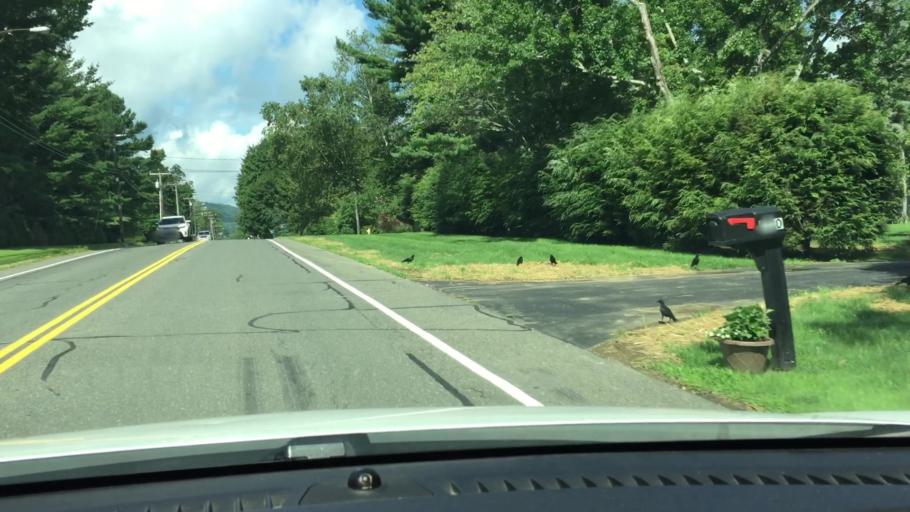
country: US
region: Massachusetts
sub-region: Berkshire County
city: Pittsfield
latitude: 42.4533
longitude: -73.2865
